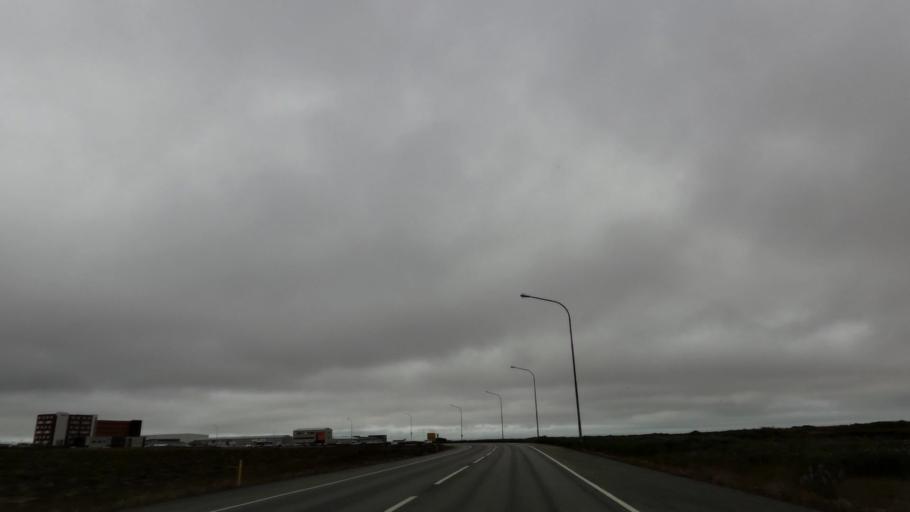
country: IS
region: Southern Peninsula
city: Reykjanesbaer
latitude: 64.0015
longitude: -22.6230
